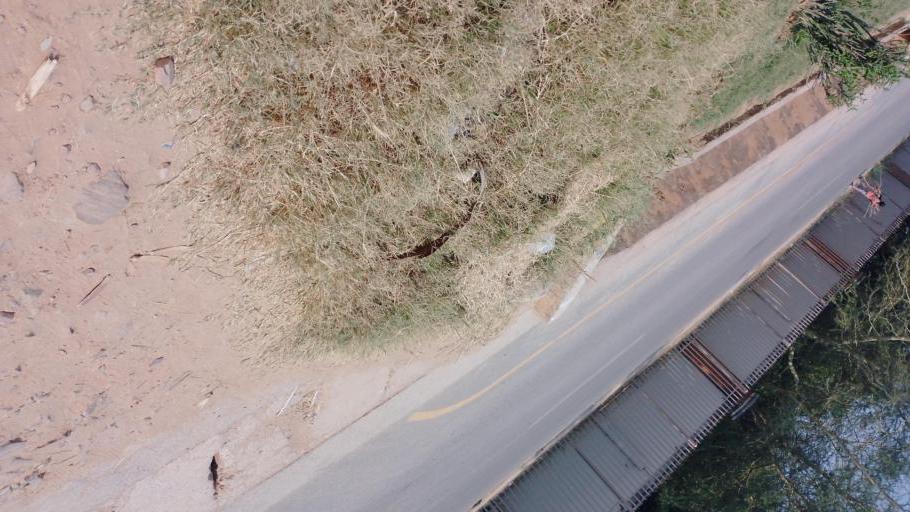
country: ZM
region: Lusaka
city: Lusaka
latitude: -15.3917
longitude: 28.3920
